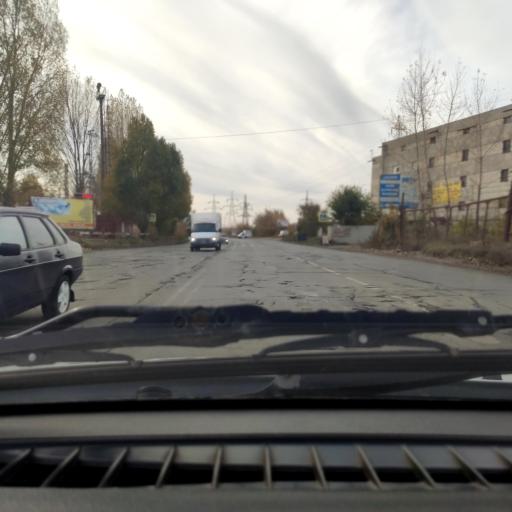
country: RU
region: Samara
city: Tol'yatti
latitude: 53.5209
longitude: 49.4683
